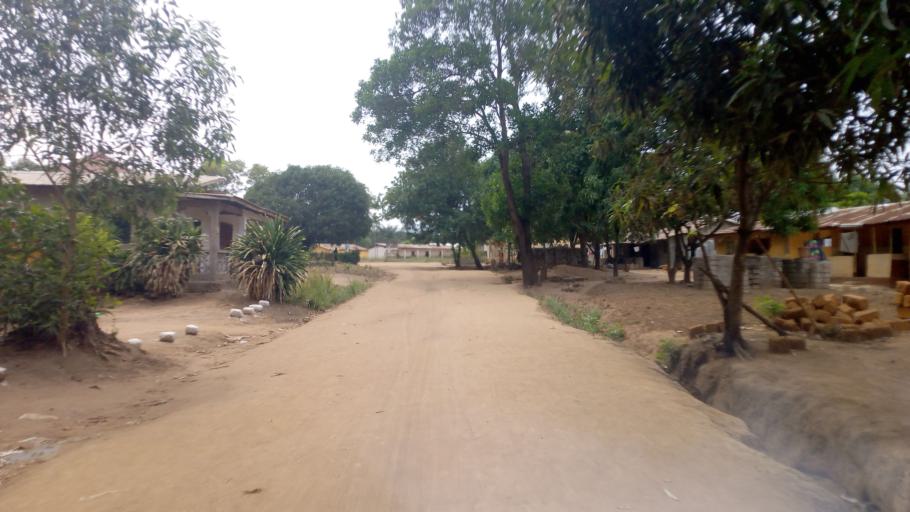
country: SL
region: Western Area
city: Waterloo
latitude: 8.3128
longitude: -13.0645
